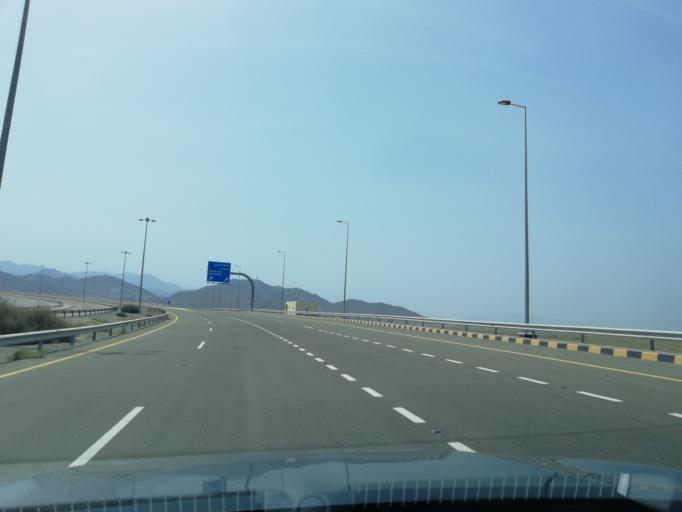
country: AE
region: Al Fujayrah
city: Al Fujayrah
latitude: 24.9523
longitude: 56.3785
